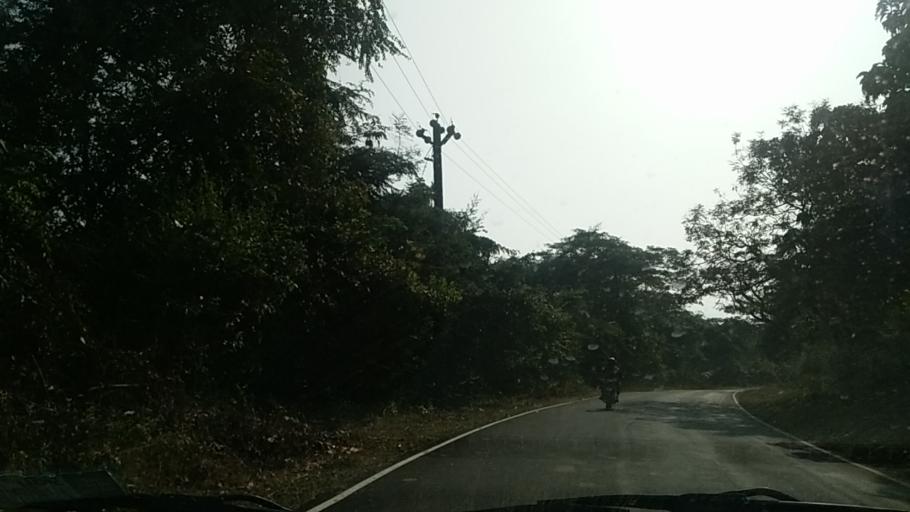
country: IN
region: Goa
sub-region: South Goa
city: Sanguem
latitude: 15.2219
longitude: 74.1945
